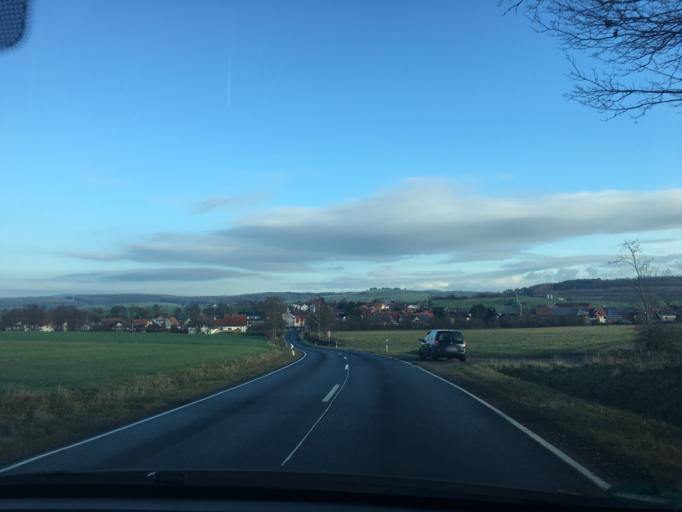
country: DE
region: Hesse
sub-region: Regierungsbezirk Kassel
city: Dipperz
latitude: 50.5766
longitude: 9.7974
